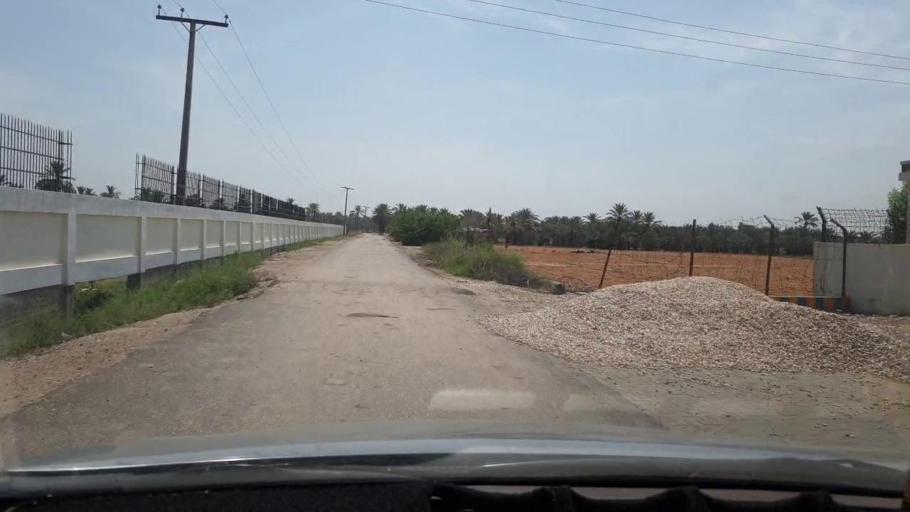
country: PK
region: Sindh
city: Khairpur
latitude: 27.4884
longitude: 68.7596
